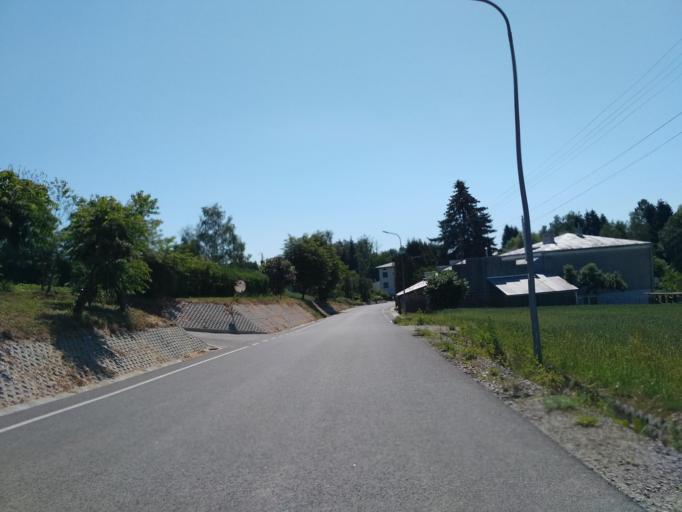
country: PL
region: Subcarpathian Voivodeship
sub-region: Powiat krosnienski
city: Korczyna
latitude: 49.7215
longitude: 21.7970
